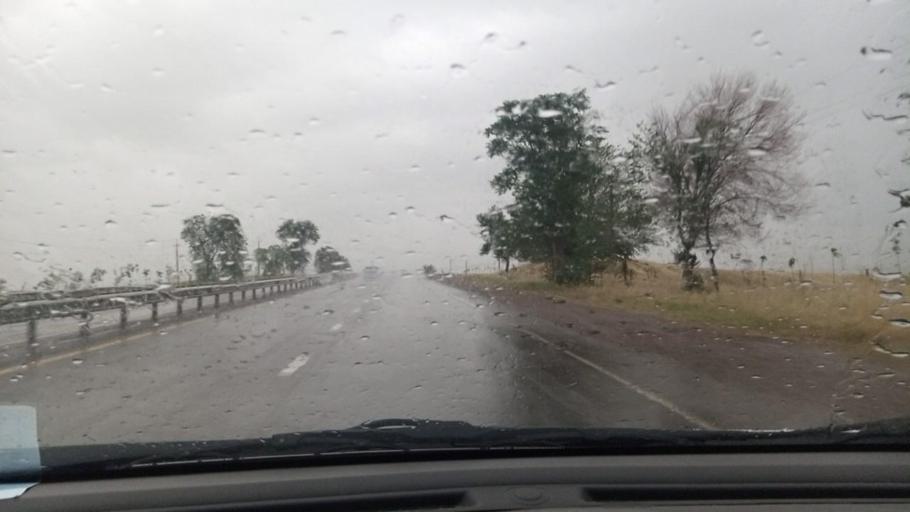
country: UZ
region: Toshkent
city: Ohangaron
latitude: 40.9504
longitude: 69.5706
